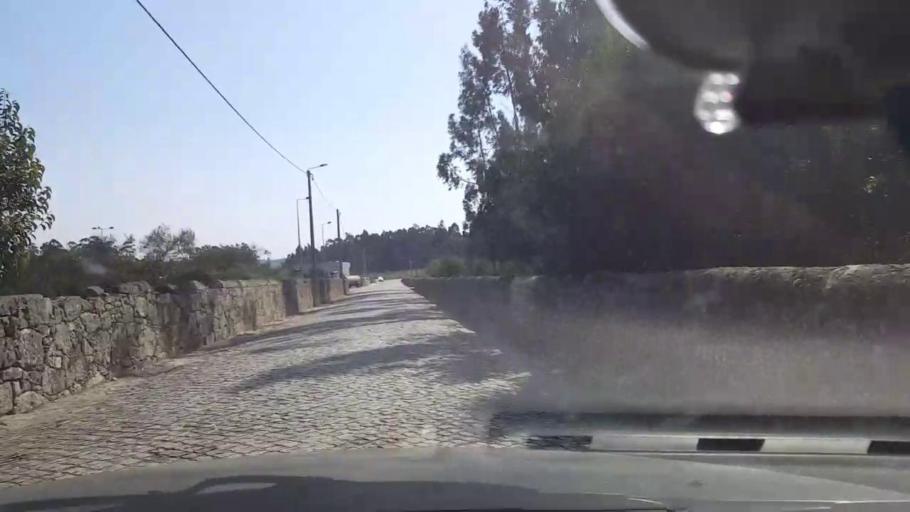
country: PT
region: Porto
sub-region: Vila do Conde
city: Vila do Conde
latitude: 41.3830
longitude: -8.7181
